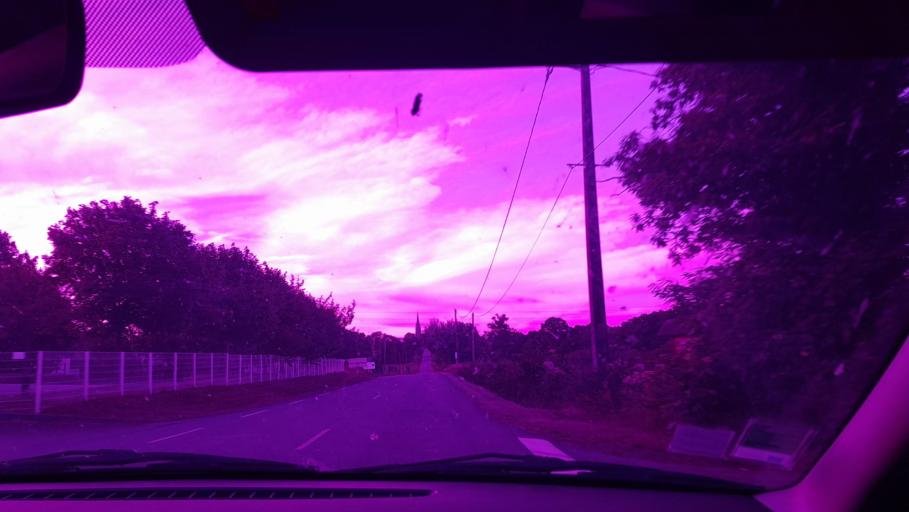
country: FR
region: Brittany
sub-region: Departement d'Ille-et-Vilaine
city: Le Pertre
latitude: 48.0205
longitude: -1.0374
